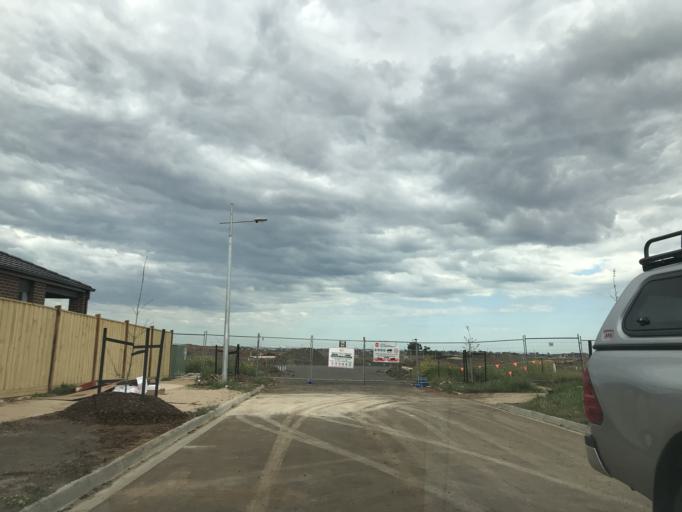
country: AU
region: Victoria
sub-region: Wyndham
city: Truganina
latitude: -37.8279
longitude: 144.7267
